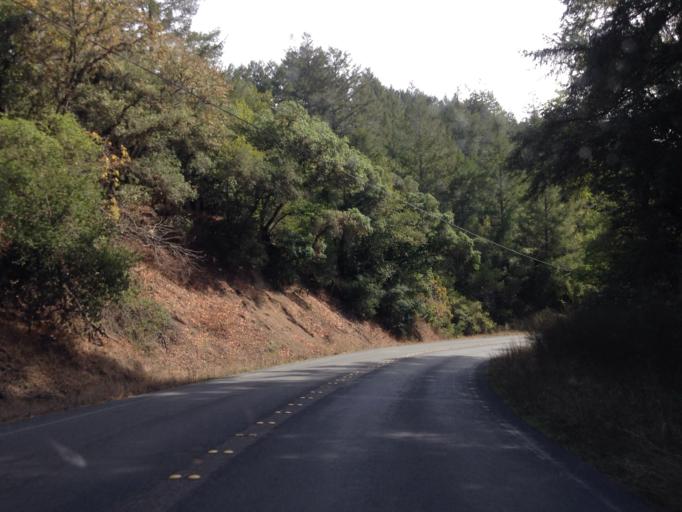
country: US
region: California
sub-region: Sonoma County
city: Occidental
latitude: 38.4167
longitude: -122.9337
